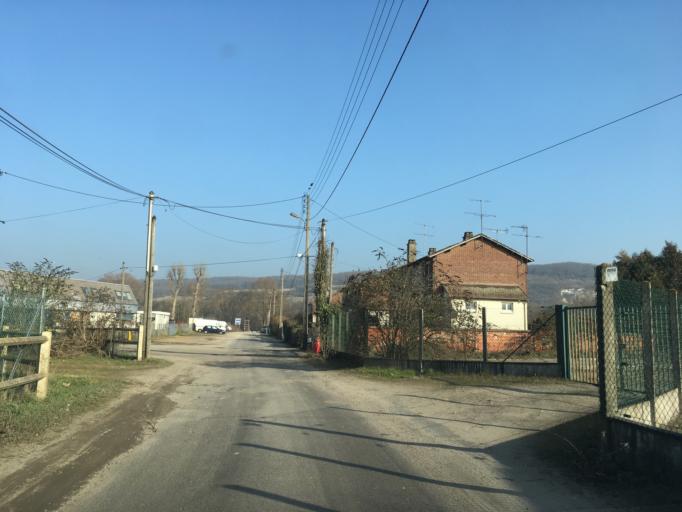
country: FR
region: Haute-Normandie
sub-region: Departement de l'Eure
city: Vernon
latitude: 49.1024
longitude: 1.4698
